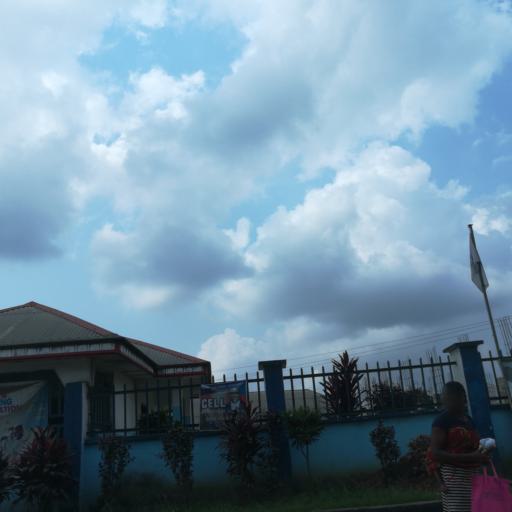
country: NG
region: Rivers
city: Okrika
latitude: 4.7974
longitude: 7.1109
